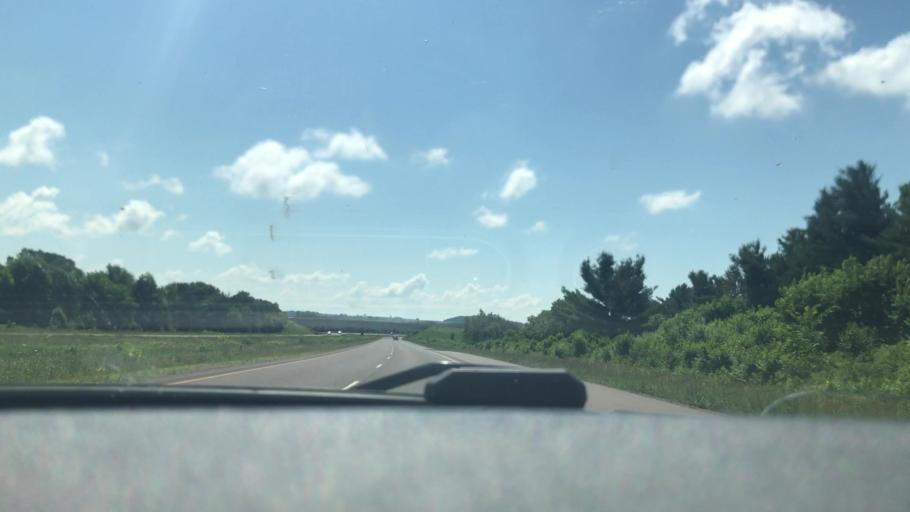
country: US
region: Wisconsin
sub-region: Chippewa County
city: Bloomer
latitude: 45.0718
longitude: -91.4735
